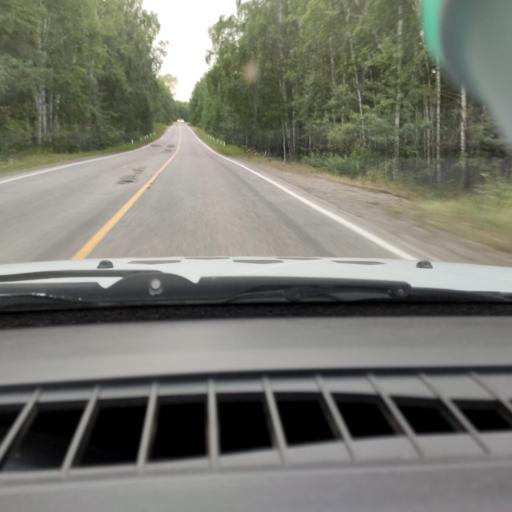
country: RU
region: Chelyabinsk
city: Ozersk
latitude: 55.8311
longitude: 60.6479
